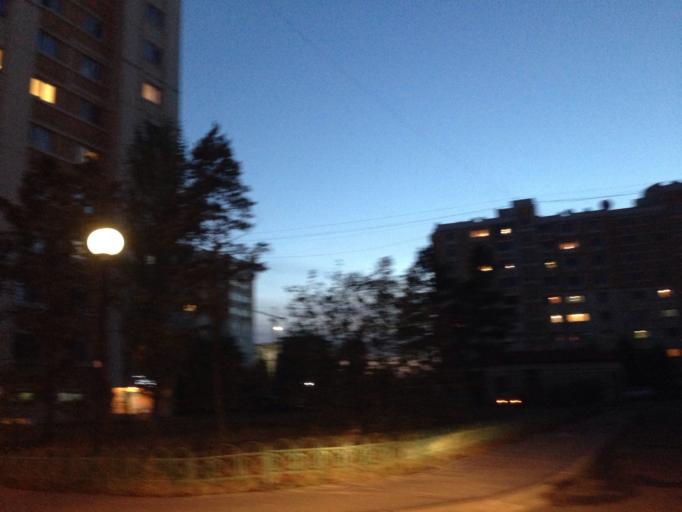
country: KZ
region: Astana Qalasy
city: Astana
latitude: 51.1560
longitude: 71.4297
